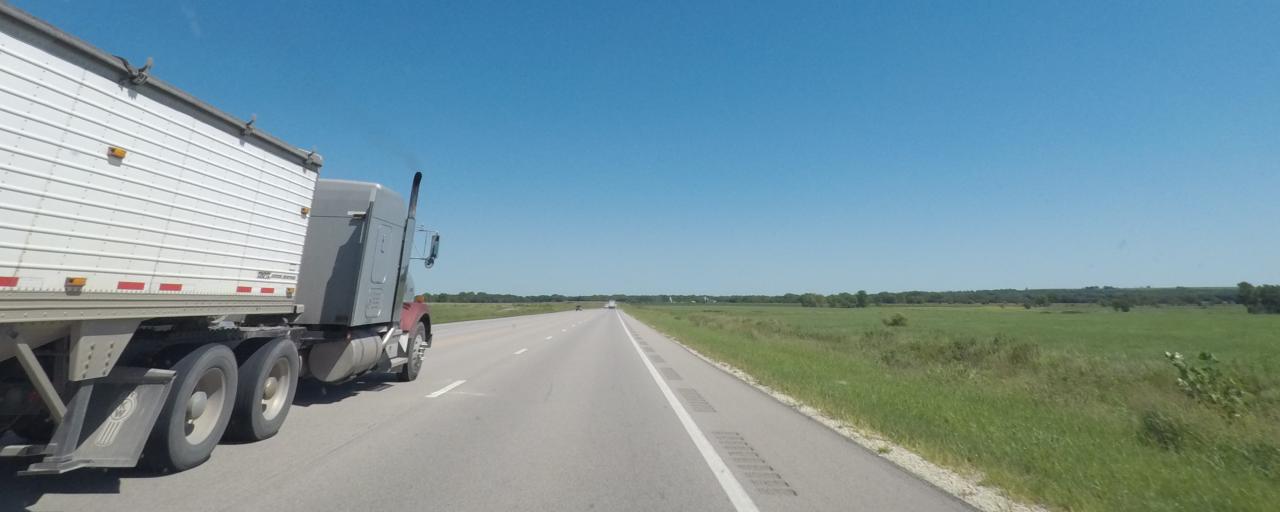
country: US
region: Kansas
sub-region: Chase County
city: Cottonwood Falls
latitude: 38.4055
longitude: -96.4140
